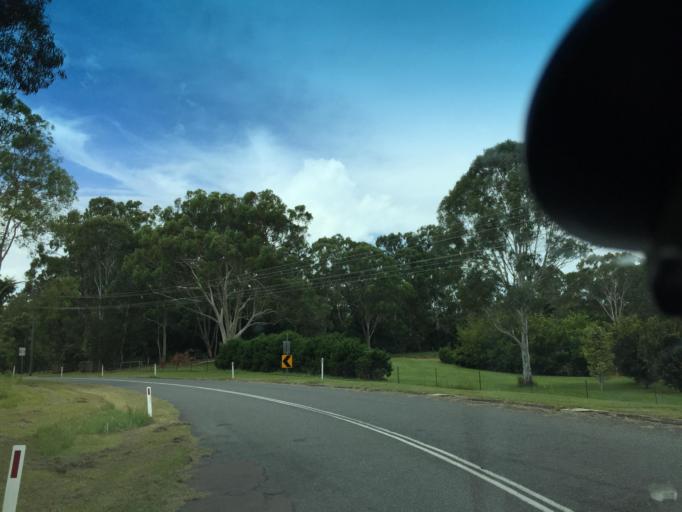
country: AU
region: Queensland
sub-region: Moreton Bay
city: Burpengary
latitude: -27.1459
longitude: 152.9614
